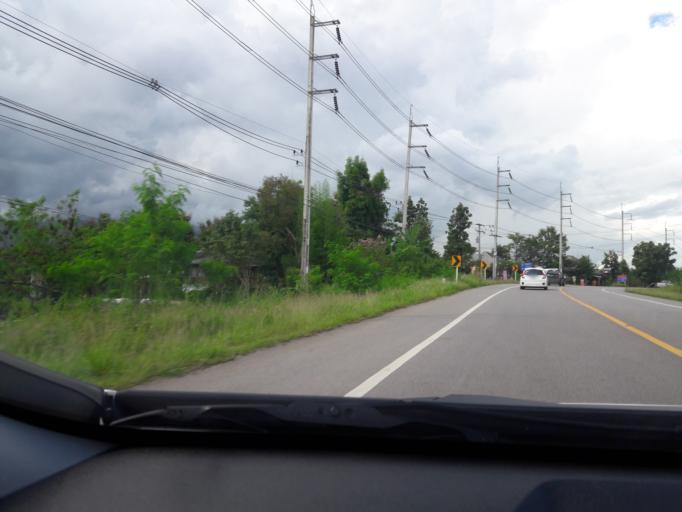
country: TH
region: Mae Hong Son
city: Mae Hi
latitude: 19.3339
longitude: 98.4321
